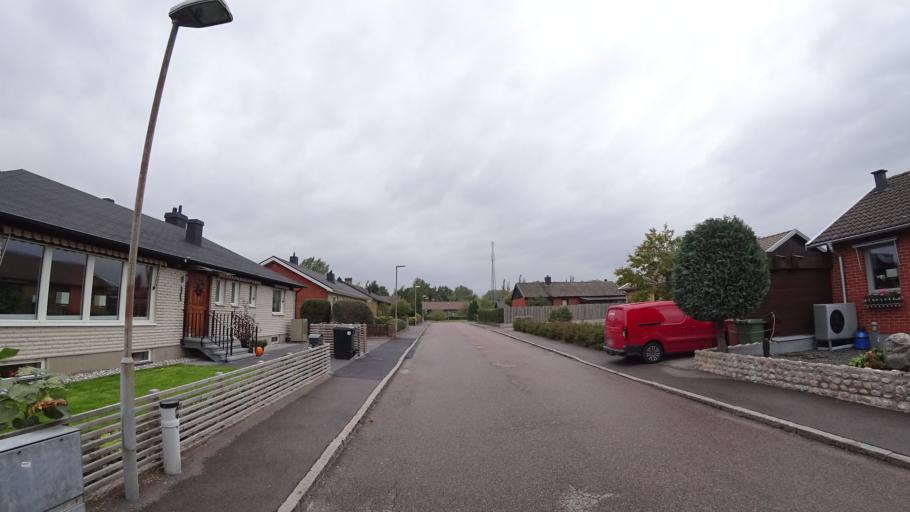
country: SE
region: Skane
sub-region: Kavlinge Kommun
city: Kaevlinge
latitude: 55.7965
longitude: 13.1249
